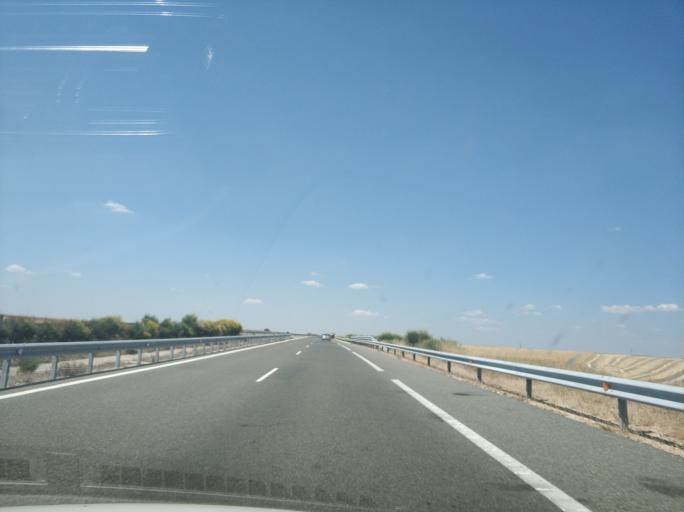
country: ES
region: Castille and Leon
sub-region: Provincia de Salamanca
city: Villamayor
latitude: 41.0138
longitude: -5.6791
